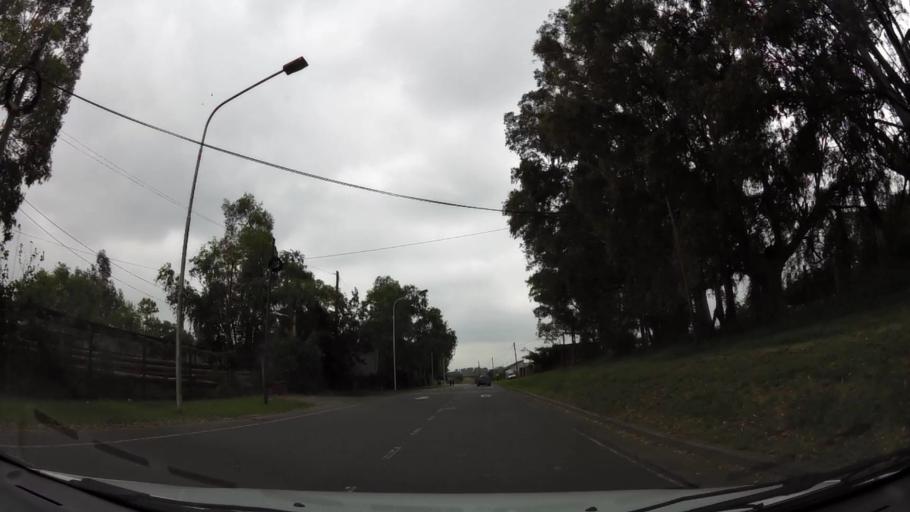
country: AR
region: Buenos Aires F.D.
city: Villa Lugano
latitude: -34.7295
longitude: -58.5152
